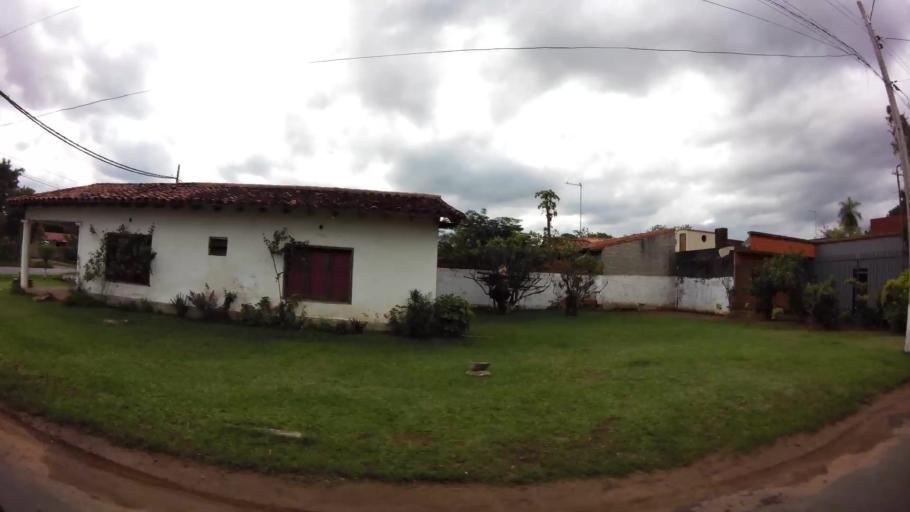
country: PY
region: Central
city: San Lorenzo
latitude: -25.2799
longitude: -57.4918
